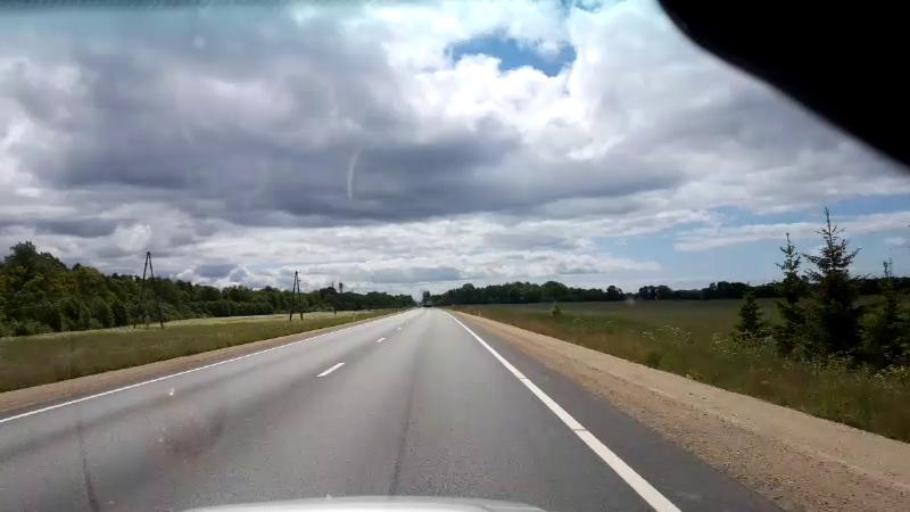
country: LV
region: Salacgrivas
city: Salacgriva
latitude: 57.7060
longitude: 24.3695
